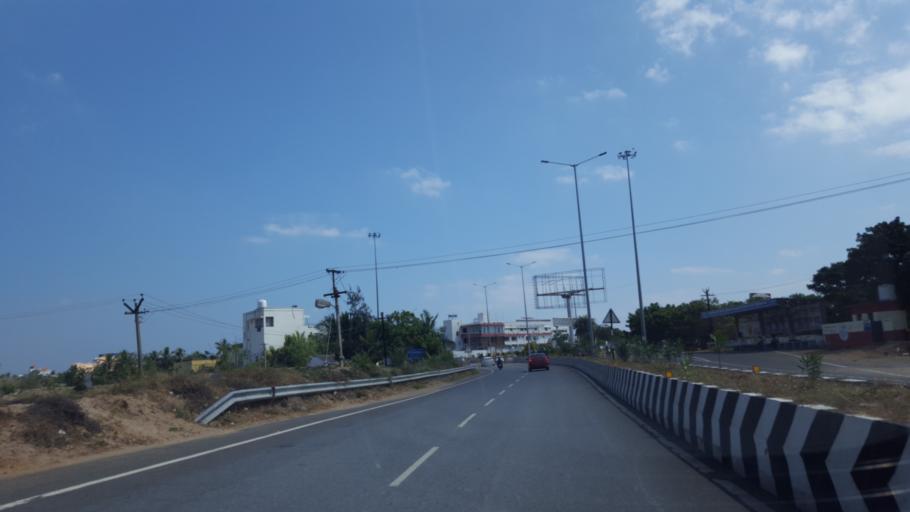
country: IN
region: Tamil Nadu
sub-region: Kancheepuram
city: Mamallapuram
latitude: 12.6274
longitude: 80.1934
